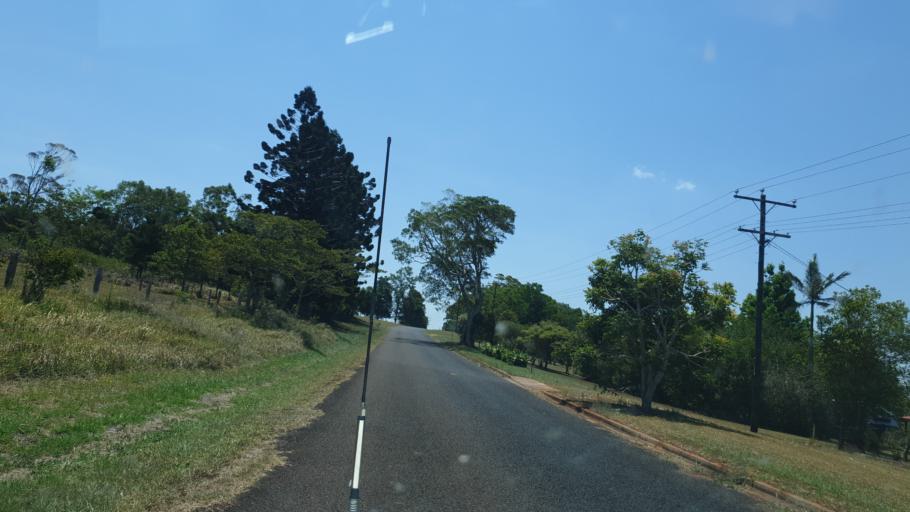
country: AU
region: Queensland
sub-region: Tablelands
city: Atherton
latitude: -17.3495
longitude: 145.6178
